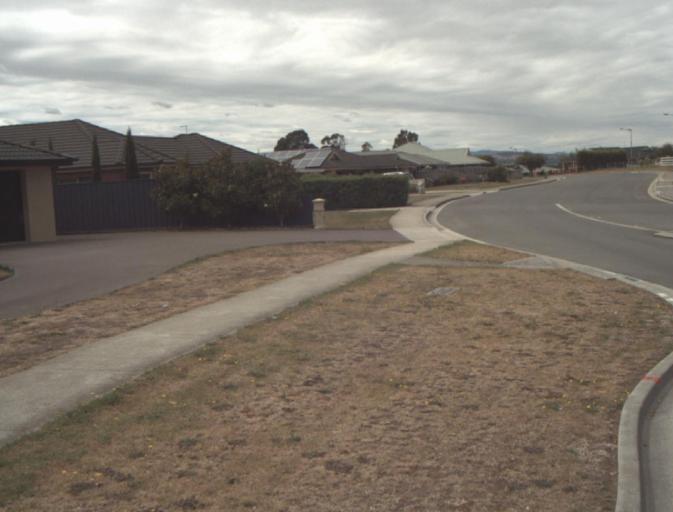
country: AU
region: Tasmania
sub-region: Launceston
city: Invermay
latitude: -41.3927
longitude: 147.1166
